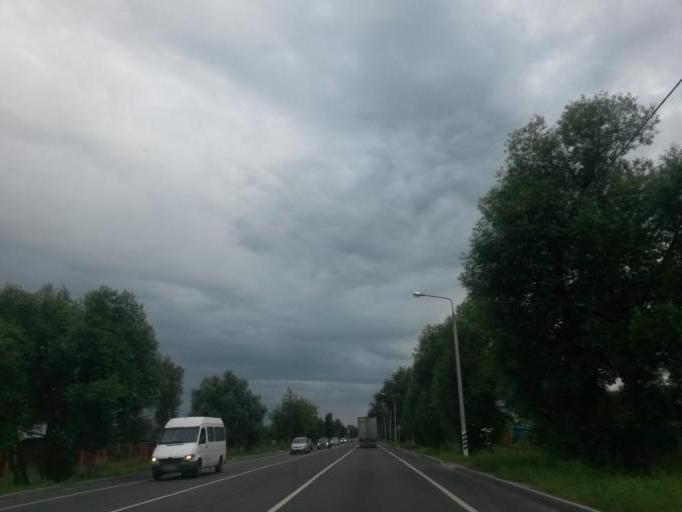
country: RU
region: Moskovskaya
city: L'vovskiy
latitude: 55.3275
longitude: 37.5284
